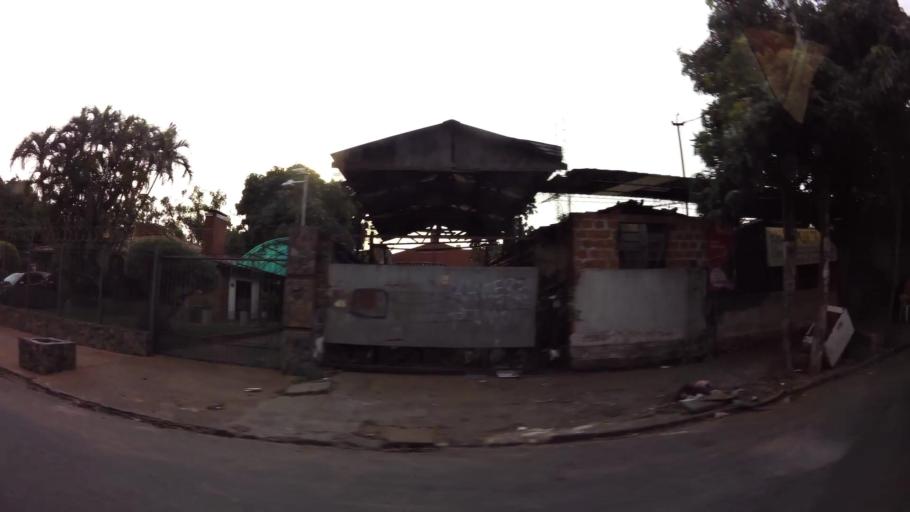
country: PY
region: Central
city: Lambare
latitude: -25.3242
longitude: -57.5744
